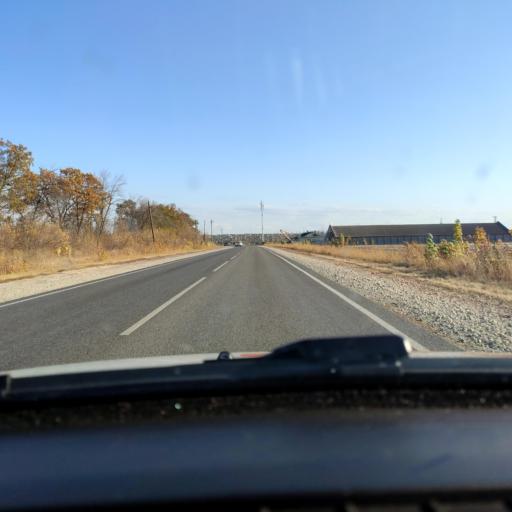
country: RU
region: Voronezj
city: Semiluki
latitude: 51.7249
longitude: 38.9912
